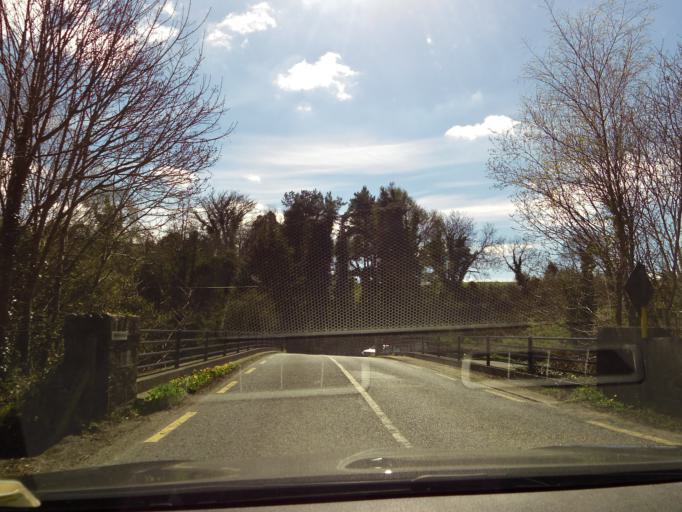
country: IE
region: Leinster
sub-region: Wicklow
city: Aughrim
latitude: 52.8498
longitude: -6.2962
